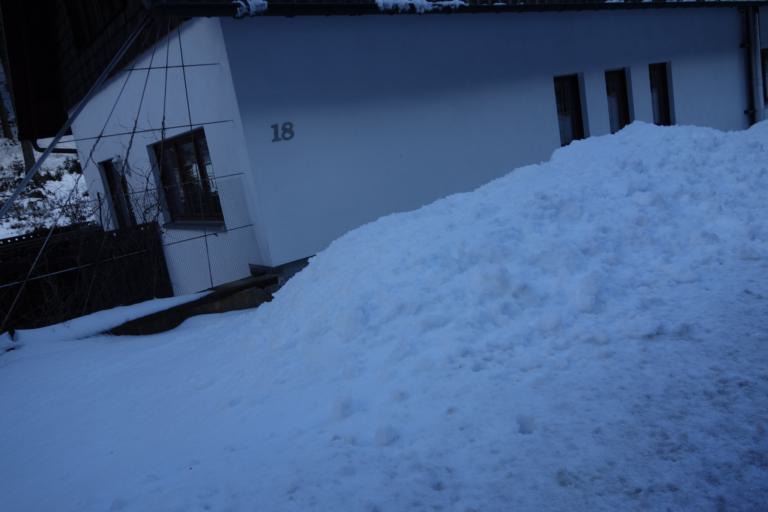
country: DE
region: Saxony
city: Eibenstock
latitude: 50.4461
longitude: 12.6251
